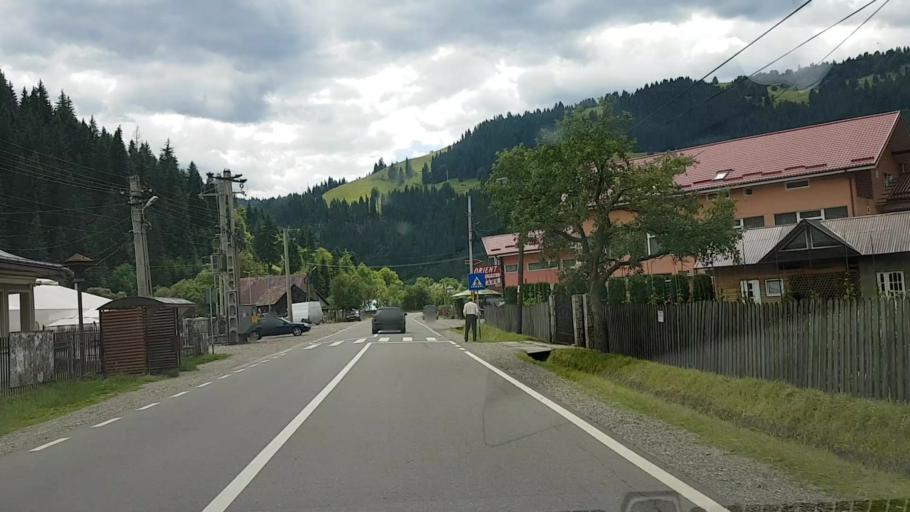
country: RO
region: Neamt
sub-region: Comuna Farcasa
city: Farcasa
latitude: 47.1465
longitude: 25.8643
